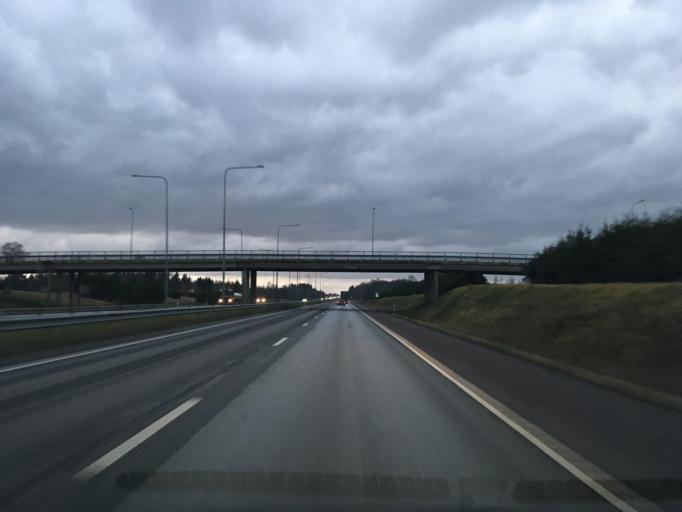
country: EE
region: Harju
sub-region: Rae vald
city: Vaida
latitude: 59.3127
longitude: 24.9354
